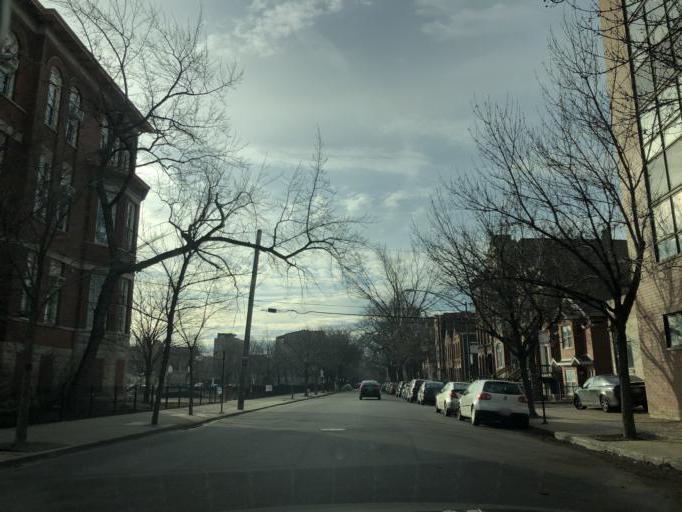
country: US
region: Illinois
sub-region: Cook County
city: Chicago
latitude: 41.9031
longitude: -87.6748
